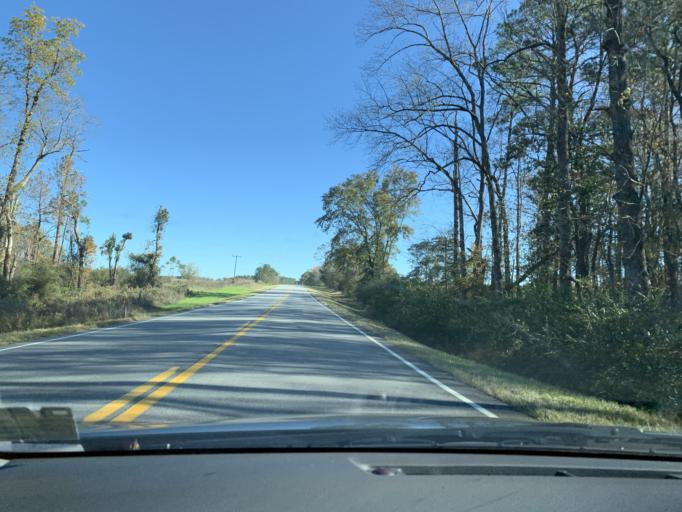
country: US
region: Georgia
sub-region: Ben Hill County
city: Fitzgerald
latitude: 31.7720
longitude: -83.0969
